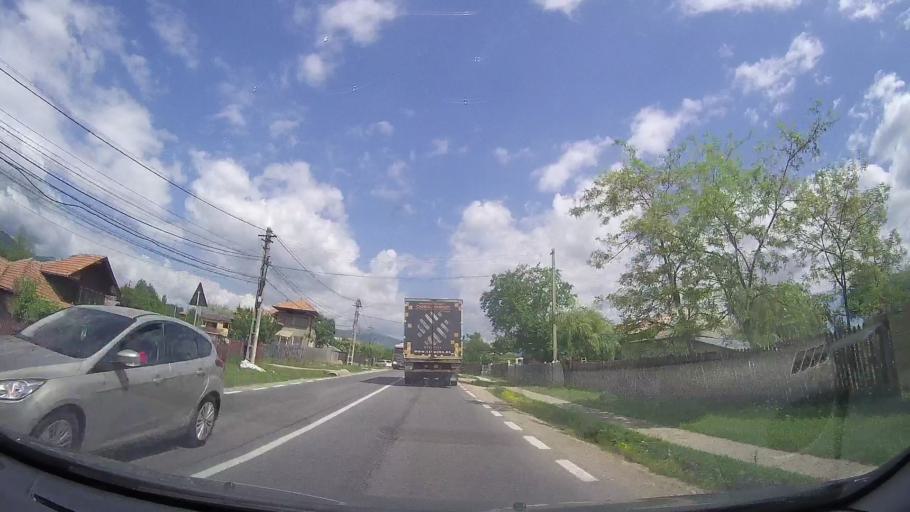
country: RO
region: Prahova
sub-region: Comuna Maneciu-Ungureni
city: Gheaba
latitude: 45.2949
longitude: 26.0002
